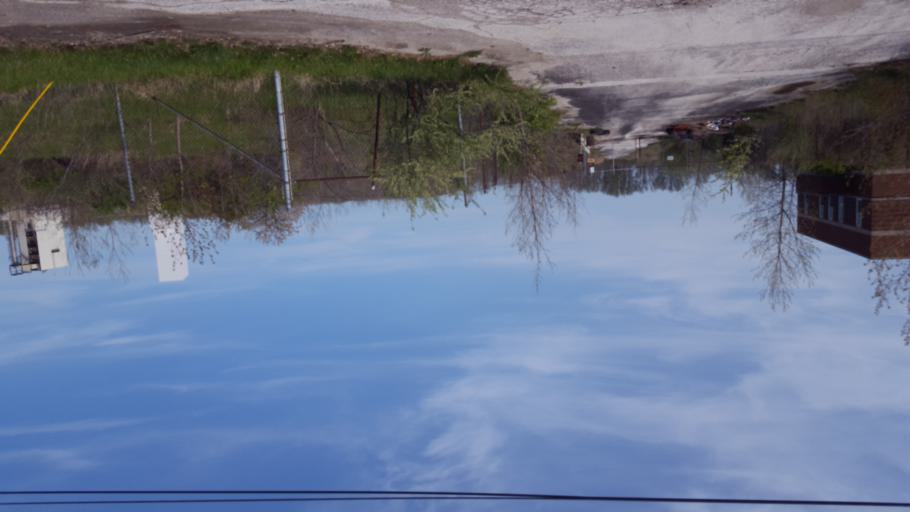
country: US
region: Ohio
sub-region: Lake County
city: Painesville
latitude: 41.7547
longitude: -81.2366
